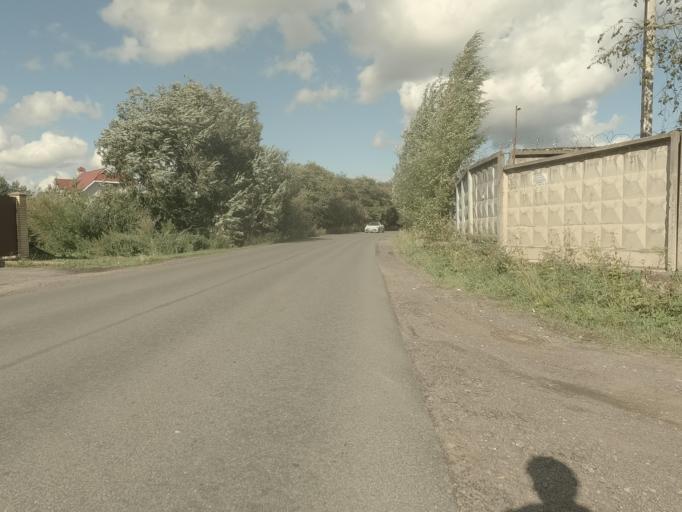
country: RU
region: Leningrad
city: Vsevolozhsk
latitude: 60.0049
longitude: 30.6436
